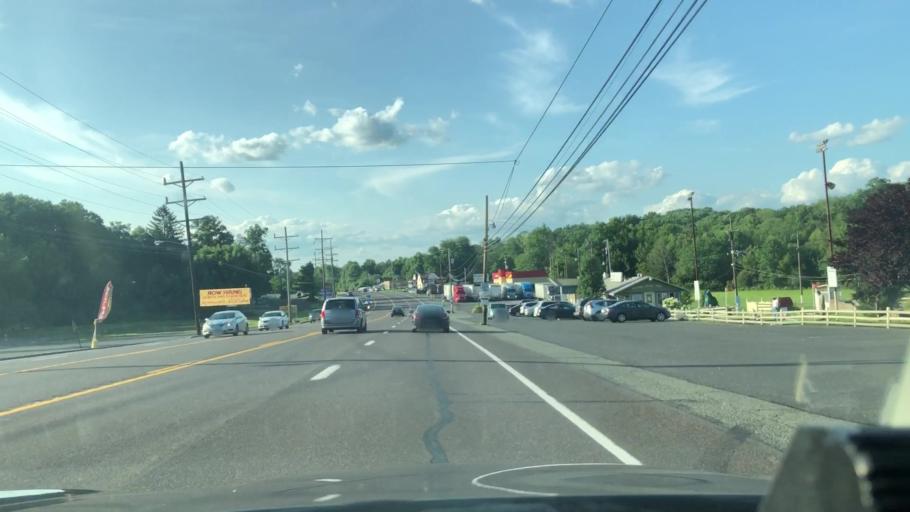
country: US
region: Pennsylvania
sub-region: Bucks County
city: Quakertown
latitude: 40.4719
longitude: -75.3706
